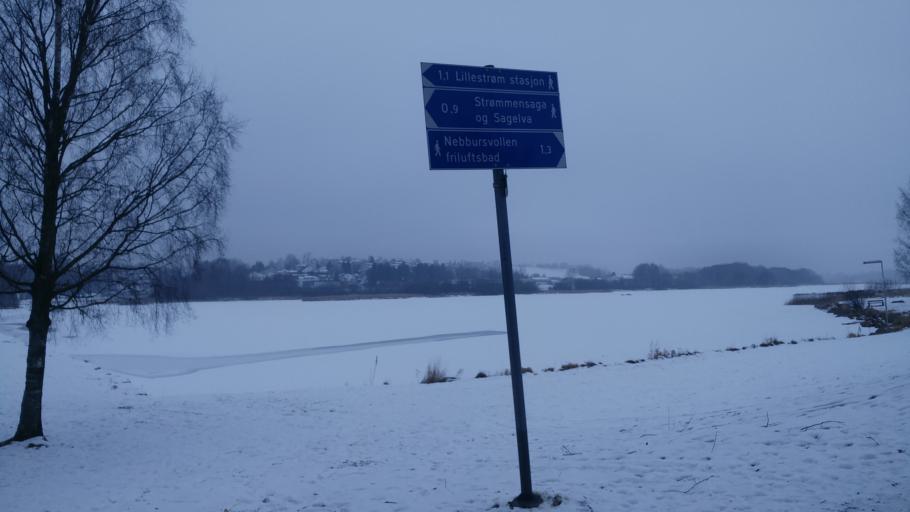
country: NO
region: Akershus
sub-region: Skedsmo
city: Lillestrom
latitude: 59.9576
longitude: 11.0300
